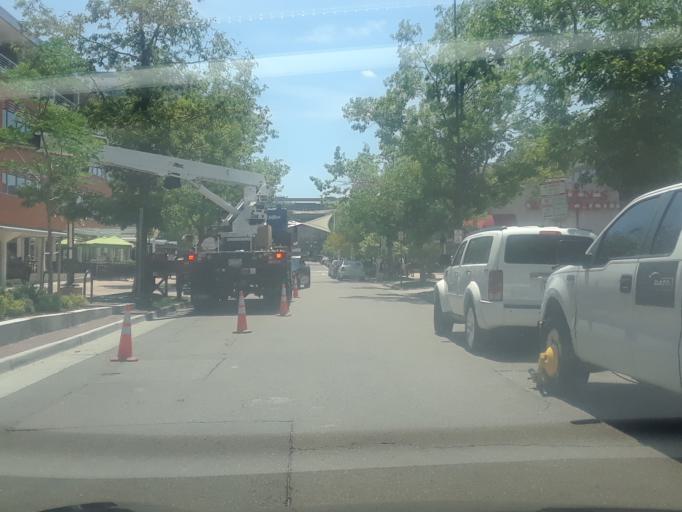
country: US
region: Colorado
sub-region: Arapahoe County
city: Glendale
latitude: 39.7203
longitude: -104.9535
